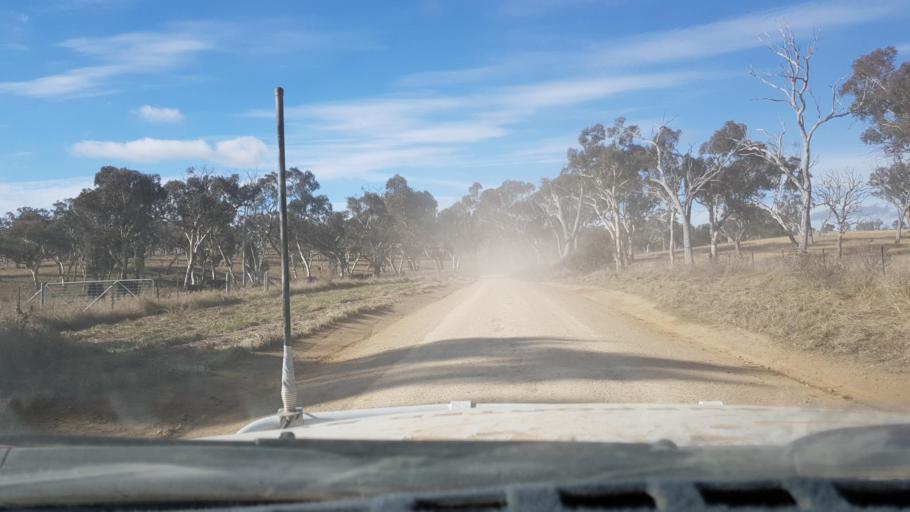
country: AU
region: New South Wales
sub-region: Armidale Dumaresq
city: Enmore
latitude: -30.7281
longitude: 151.5941
